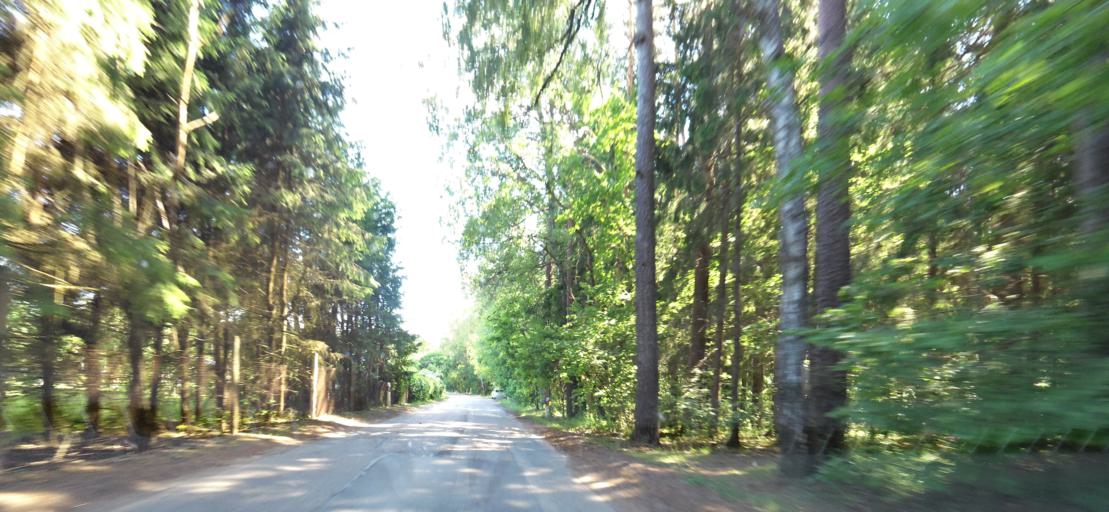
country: LT
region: Vilnius County
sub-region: Vilnius
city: Fabijoniskes
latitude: 54.8205
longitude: 25.3207
